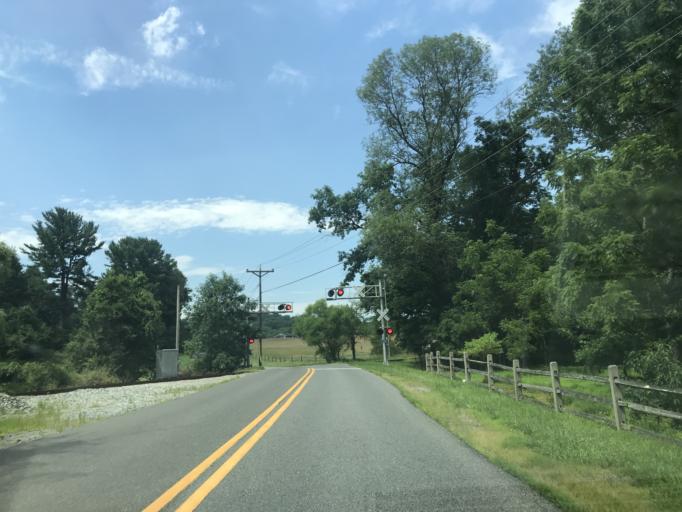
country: US
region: Delaware
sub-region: New Castle County
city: Greenville
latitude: 39.7762
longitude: -75.6405
